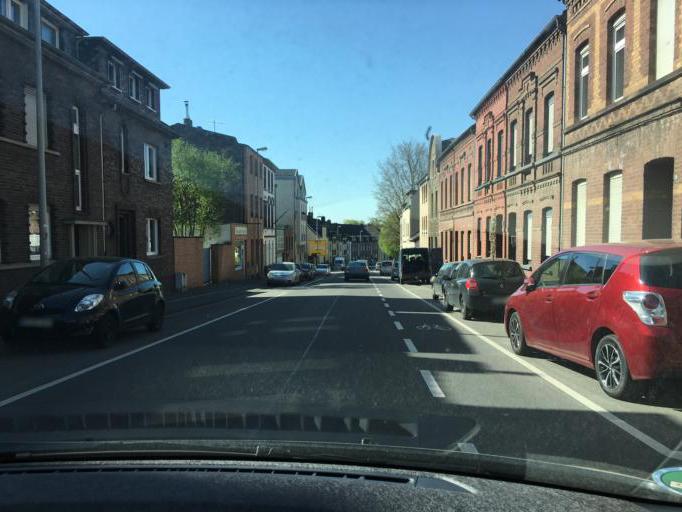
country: DE
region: North Rhine-Westphalia
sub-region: Regierungsbezirk Dusseldorf
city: Monchengladbach
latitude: 51.1518
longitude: 6.4339
